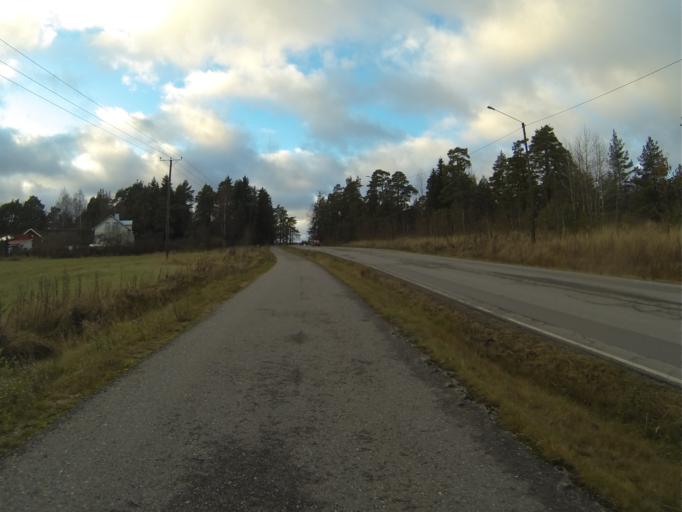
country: FI
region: Varsinais-Suomi
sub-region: Salo
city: Halikko
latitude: 60.3977
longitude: 23.0617
